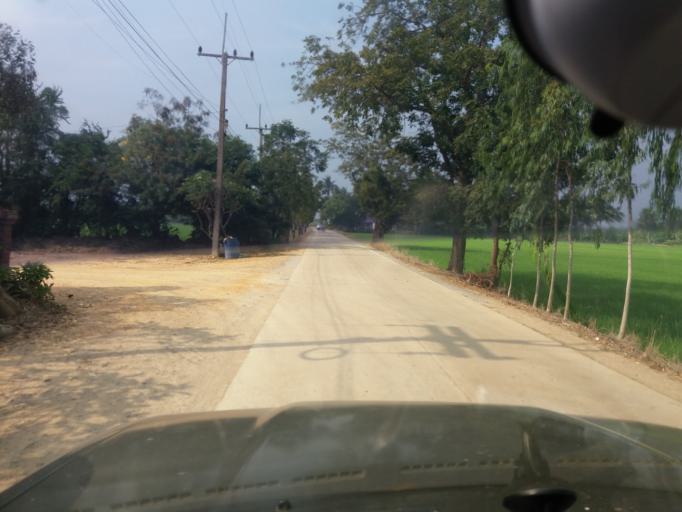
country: TH
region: Suphan Buri
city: Doem Bang Nang Buat
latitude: 14.8933
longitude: 100.1929
